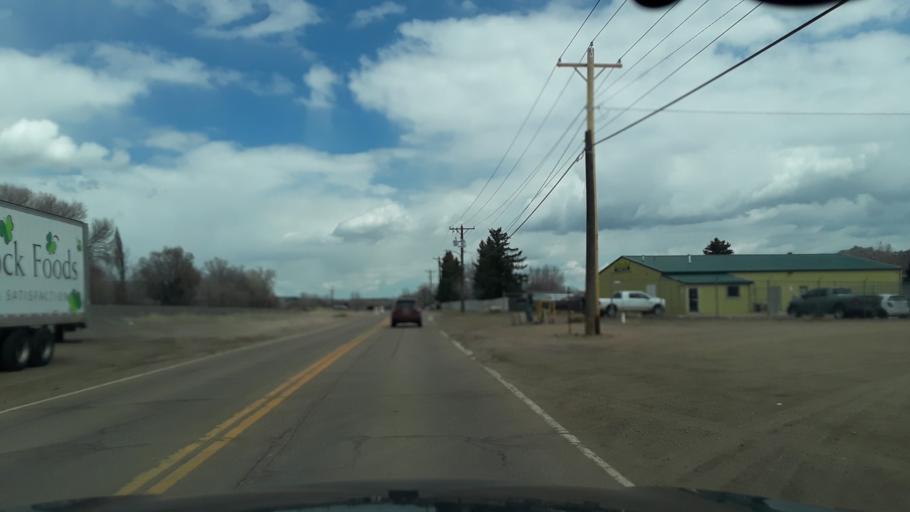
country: US
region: Colorado
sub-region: El Paso County
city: Colorado Springs
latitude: 38.8996
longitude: -104.8250
